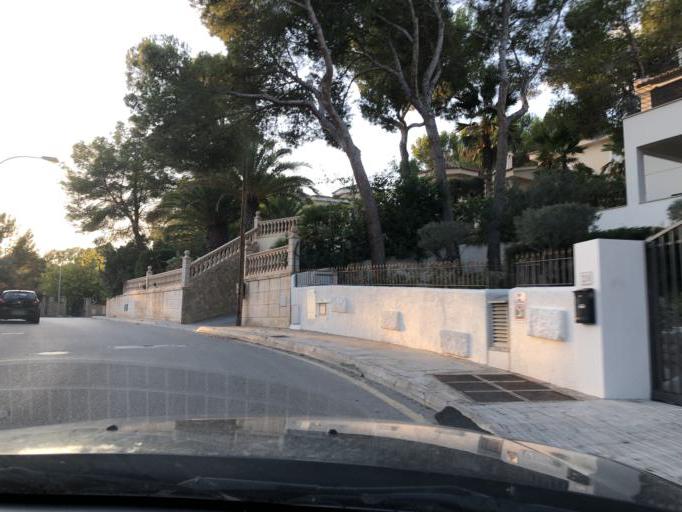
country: ES
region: Balearic Islands
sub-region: Illes Balears
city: Santa Ponsa
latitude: 39.5280
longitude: 2.4775
